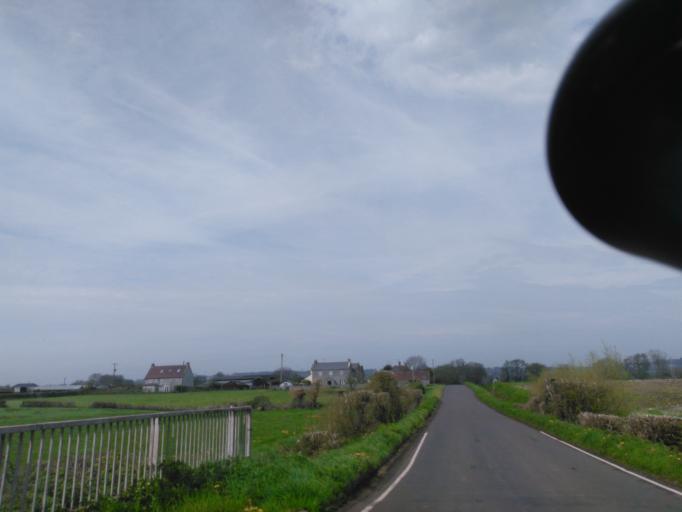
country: GB
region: England
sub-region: Somerset
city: Langport
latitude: 51.1080
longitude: -2.8197
